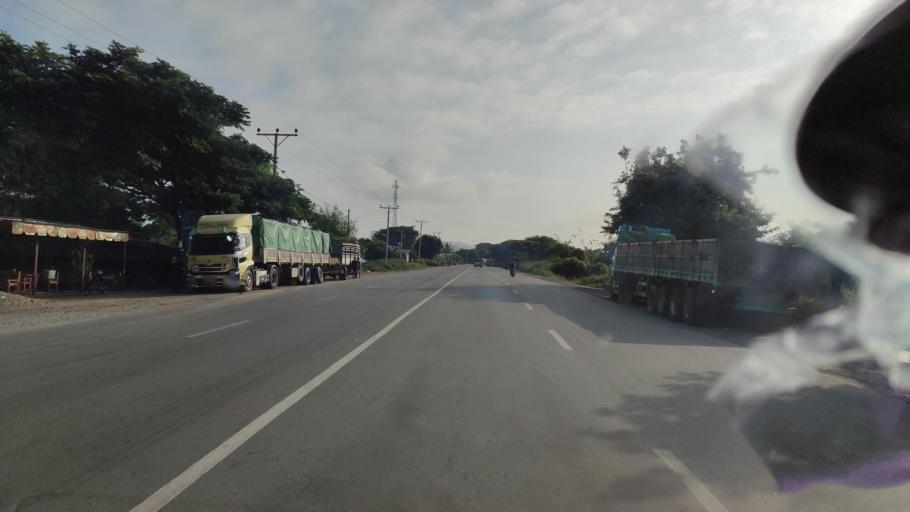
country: MM
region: Mandalay
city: Yamethin
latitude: 20.7540
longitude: 96.2493
